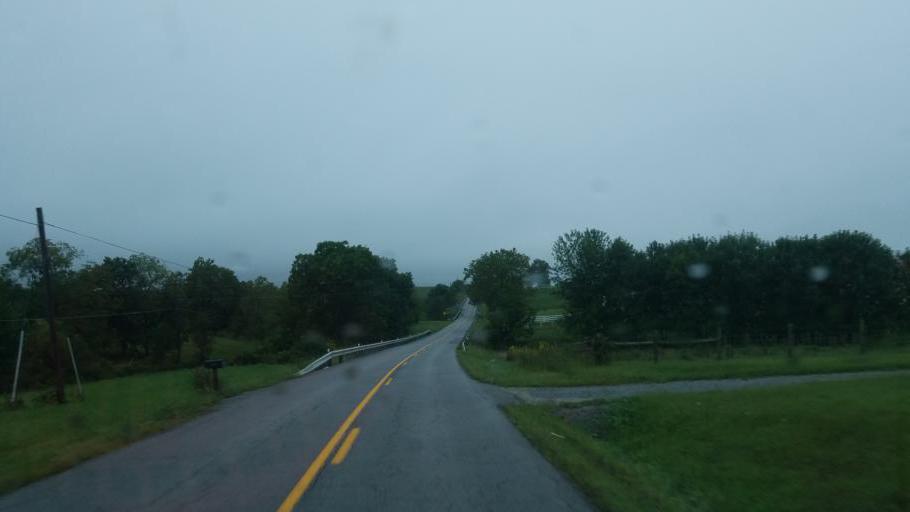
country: US
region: Kentucky
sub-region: Fleming County
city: Flemingsburg
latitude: 38.4140
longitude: -83.6781
